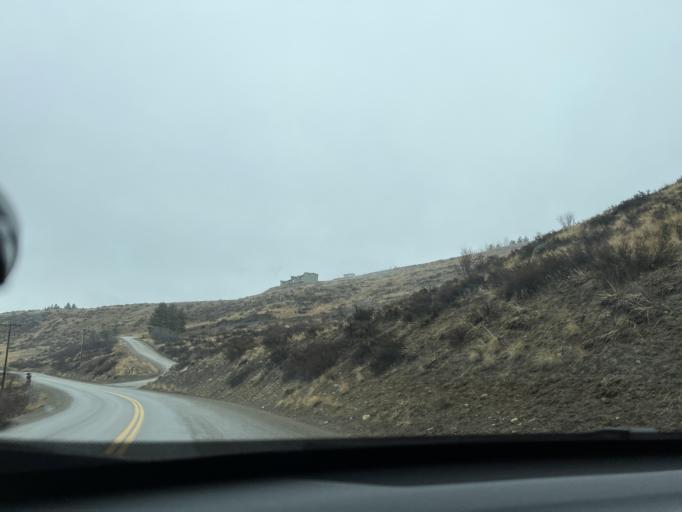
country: US
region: Washington
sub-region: Okanogan County
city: Brewster
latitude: 48.4857
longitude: -120.1776
